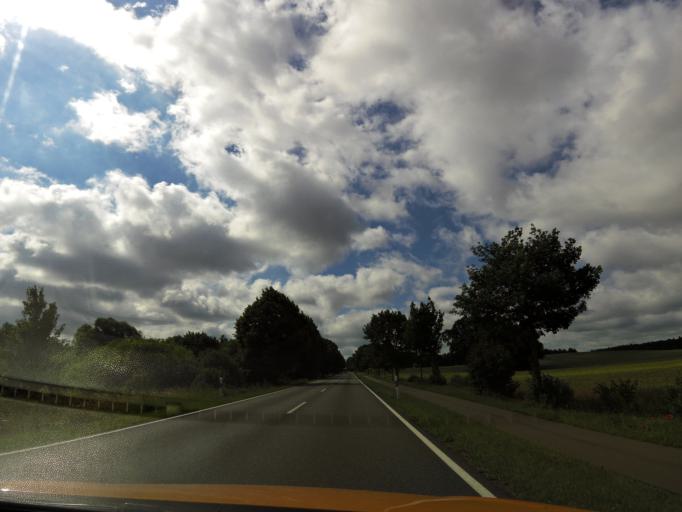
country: DE
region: Mecklenburg-Vorpommern
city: Krakow am See
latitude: 53.6817
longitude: 12.2678
